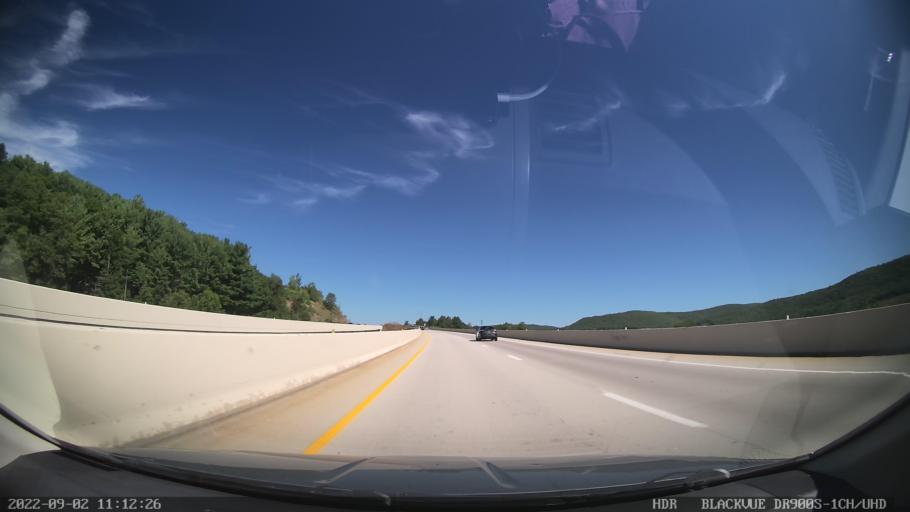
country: US
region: Pennsylvania
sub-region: Tioga County
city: Mansfield
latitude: 41.9381
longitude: -77.1108
